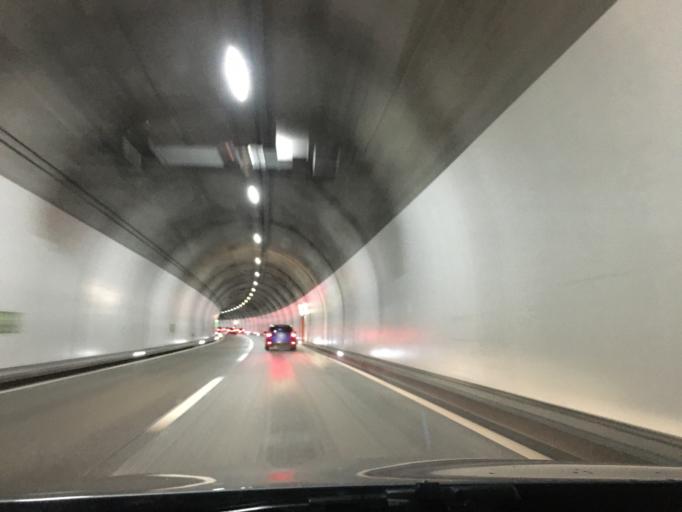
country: CH
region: Saint Gallen
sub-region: Wahlkreis Sarganserland
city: Walenstadt
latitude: 47.1136
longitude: 9.3051
